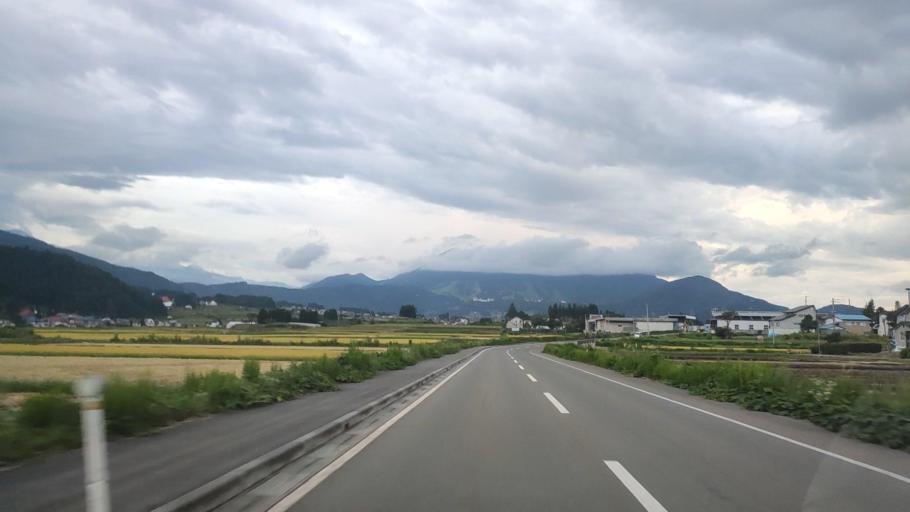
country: JP
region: Nagano
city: Iiyama
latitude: 36.8766
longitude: 138.4095
